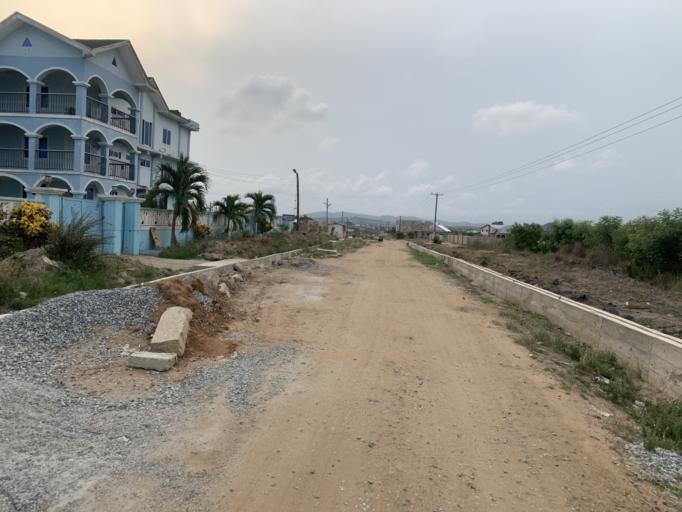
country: GH
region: Central
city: Winneba
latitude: 5.3825
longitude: -0.6264
